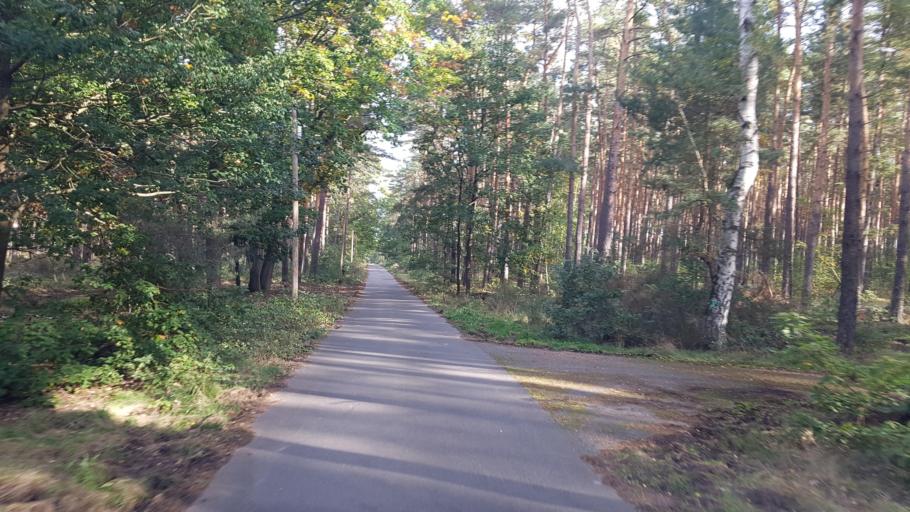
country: DE
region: Brandenburg
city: Hohenbucko
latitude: 51.8305
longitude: 13.5319
